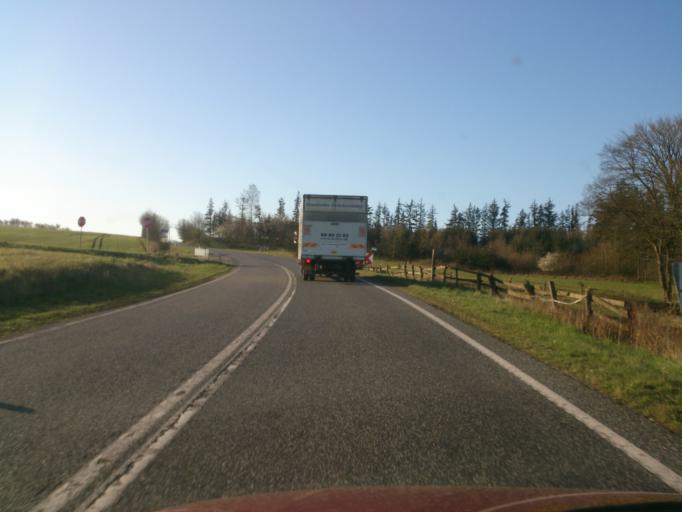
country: DK
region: Central Jutland
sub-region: Viborg Kommune
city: Bjerringbro
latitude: 56.4193
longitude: 9.6700
